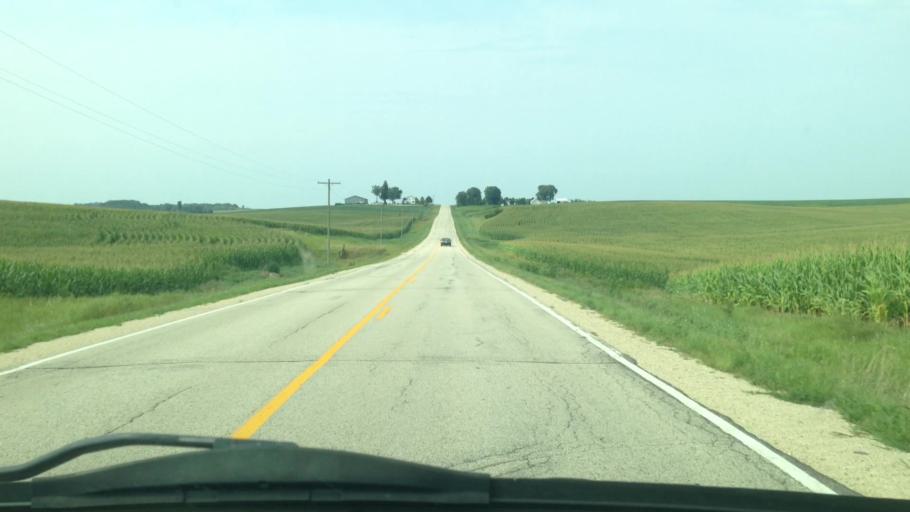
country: US
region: Minnesota
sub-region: Winona County
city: Lewiston
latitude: 43.8853
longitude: -91.9594
